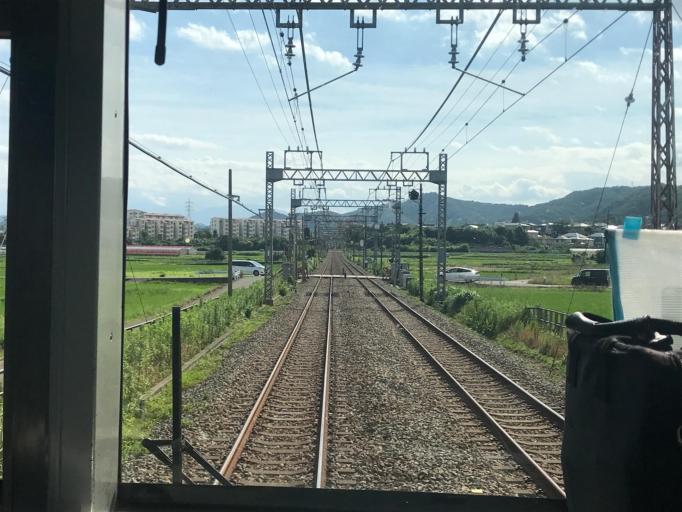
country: JP
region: Kanagawa
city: Isehara
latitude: 35.3864
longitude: 139.2896
